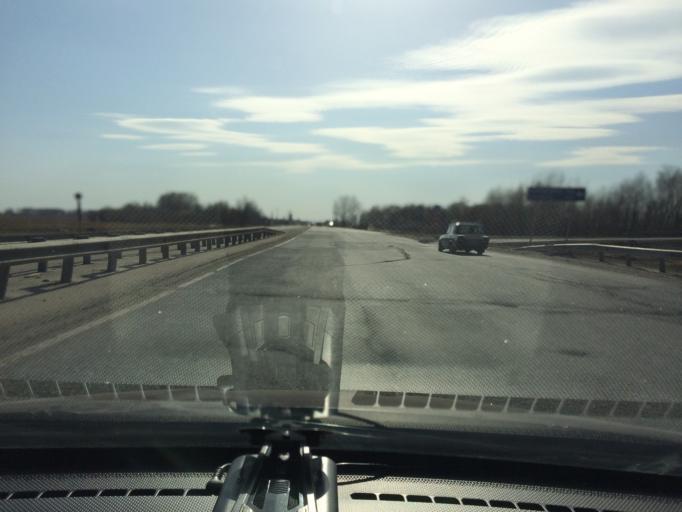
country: RU
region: Mariy-El
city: Yoshkar-Ola
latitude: 56.6793
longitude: 48.0224
